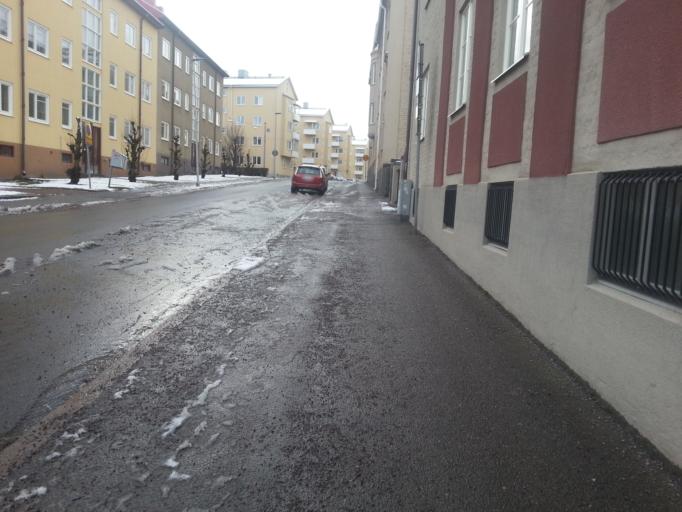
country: SE
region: OEstergoetland
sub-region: Norrkopings Kommun
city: Norrkoping
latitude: 58.5824
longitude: 16.1891
